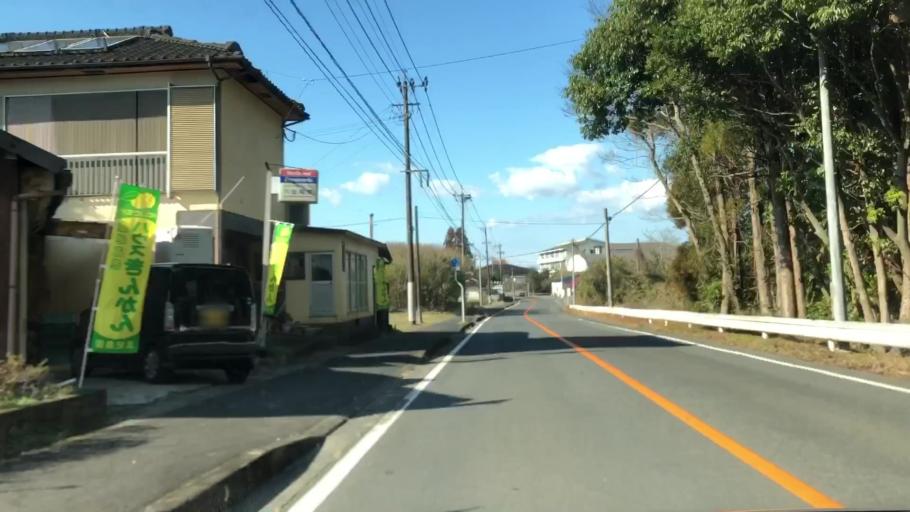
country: JP
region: Kagoshima
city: Satsumasendai
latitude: 31.7995
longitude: 130.4385
